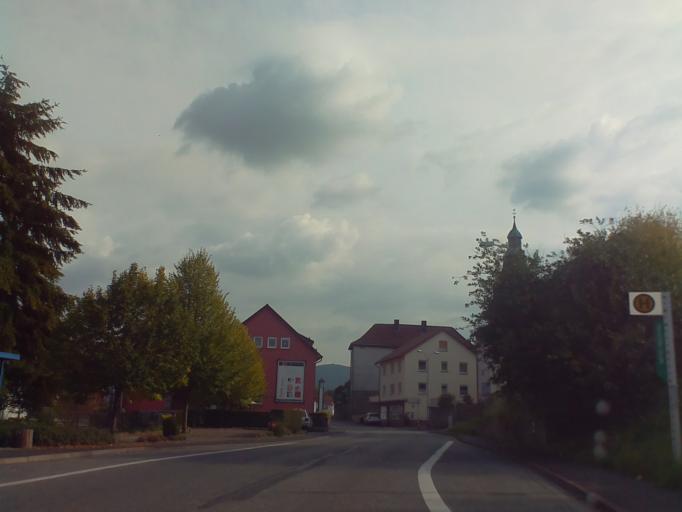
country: DE
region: Hesse
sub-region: Regierungsbezirk Kassel
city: Schenklengsfeld
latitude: 50.8193
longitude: 9.8434
